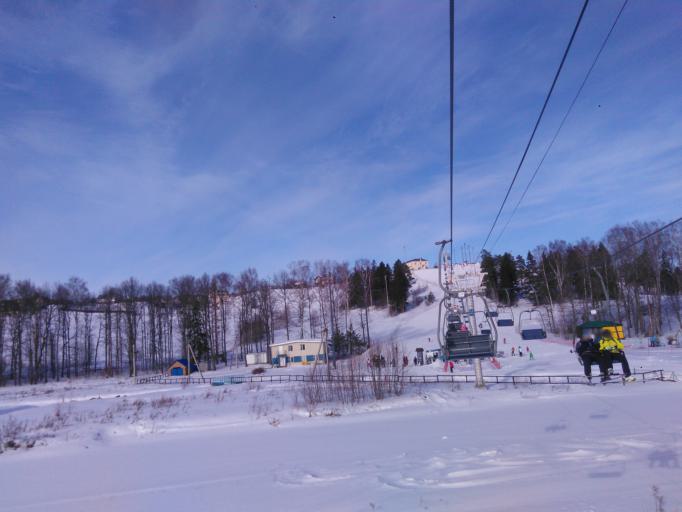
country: RU
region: Moskovskaya
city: Dedenevo
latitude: 56.2688
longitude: 37.5608
